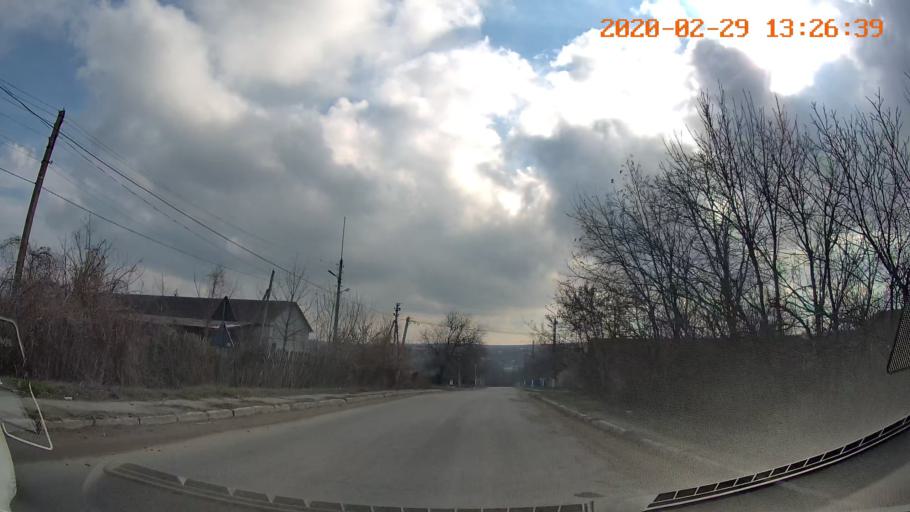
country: MD
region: Telenesti
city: Camenca
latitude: 47.9184
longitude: 28.6386
